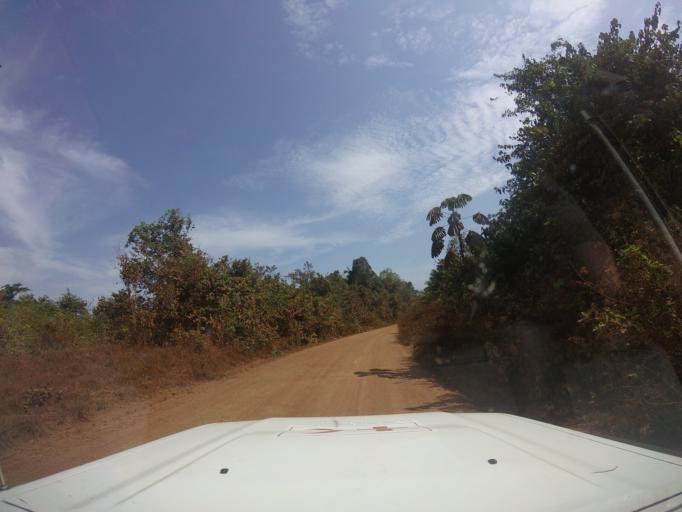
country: LR
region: Grand Cape Mount
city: Robertsport
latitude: 6.7233
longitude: -11.3361
